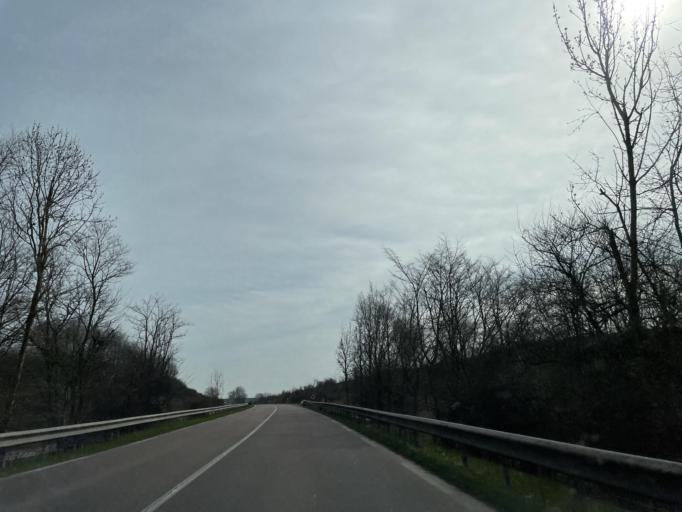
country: FR
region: Champagne-Ardenne
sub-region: Departement de l'Aube
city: Nogent-sur-Seine
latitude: 48.4833
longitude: 3.4888
